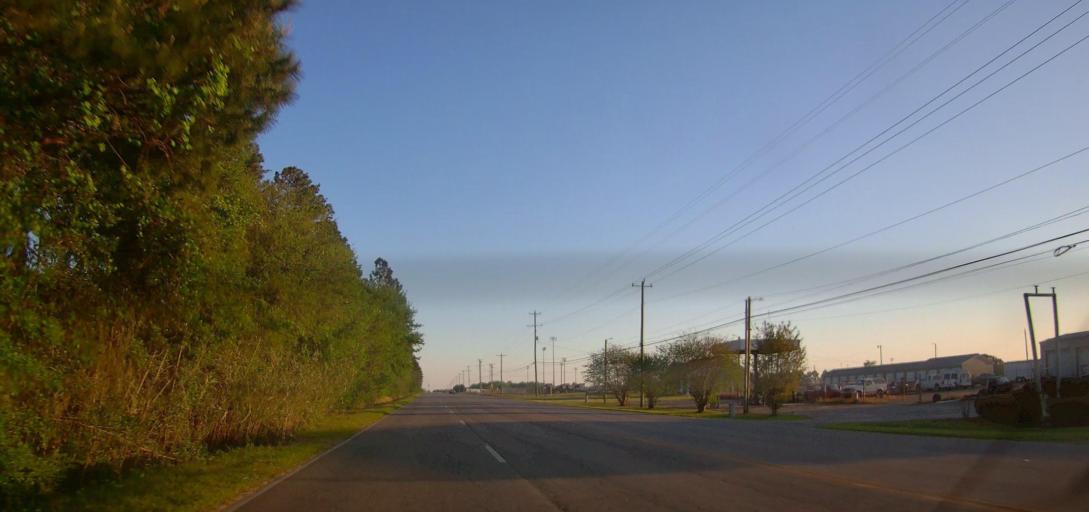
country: US
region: Georgia
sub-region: Ben Hill County
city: Fitzgerald
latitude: 31.6906
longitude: -83.2611
